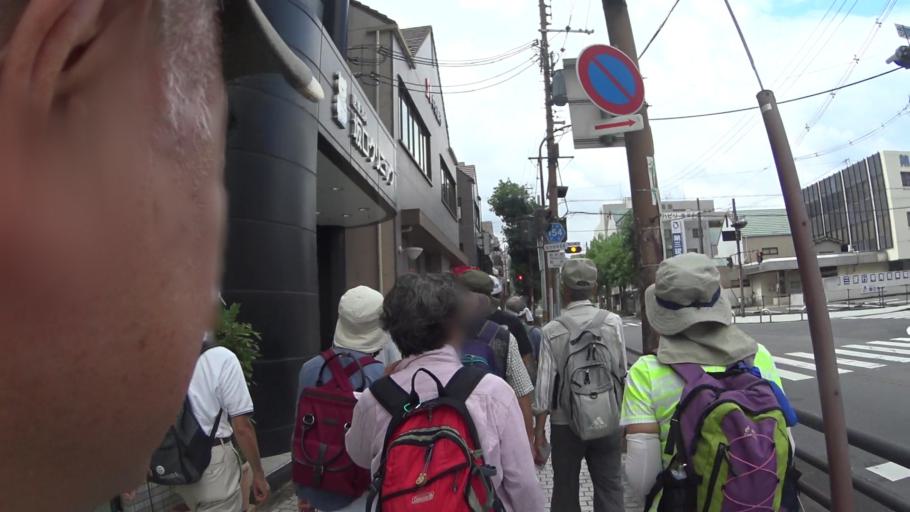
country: JP
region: Nara
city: Sakurai
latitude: 34.5108
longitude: 135.8471
